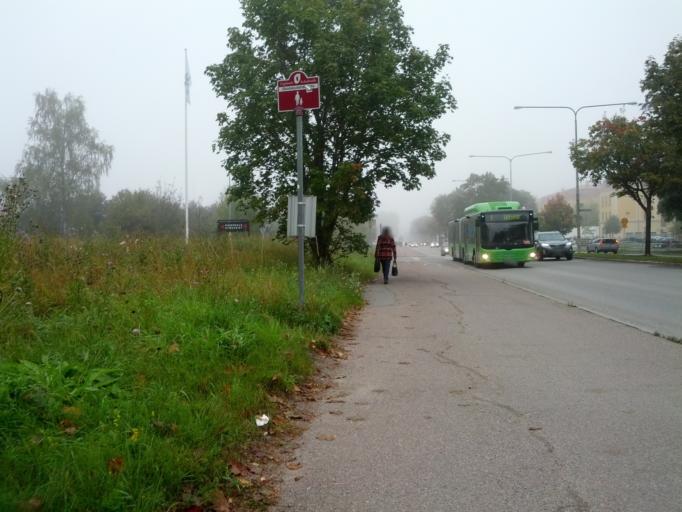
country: SE
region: Uppsala
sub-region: Uppsala Kommun
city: Uppsala
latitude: 59.8411
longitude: 17.6391
